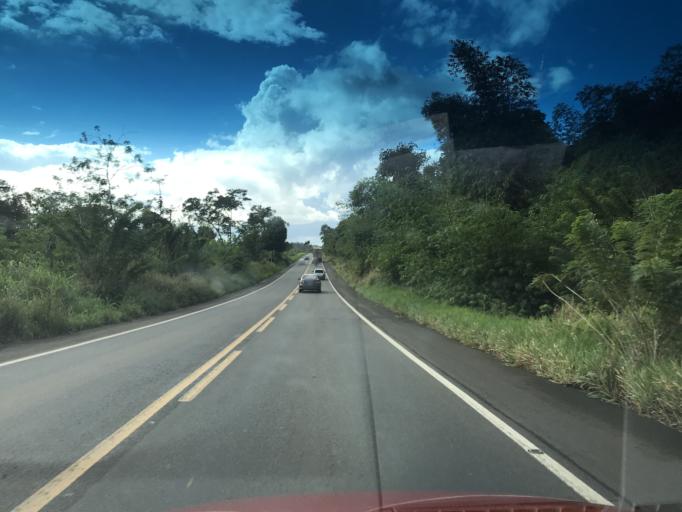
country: BR
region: Bahia
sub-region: Ibirapitanga
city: Ibirapitanga
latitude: -14.1680
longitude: -39.3281
